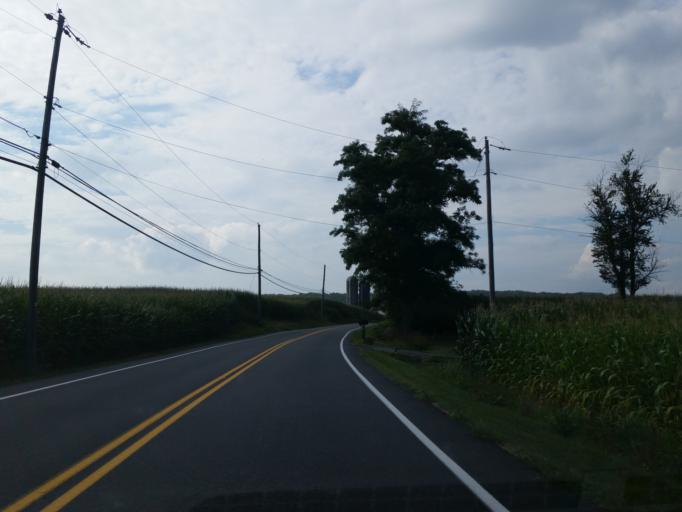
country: US
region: Pennsylvania
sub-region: Lancaster County
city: Mount Joy
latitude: 40.2090
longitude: -76.5046
